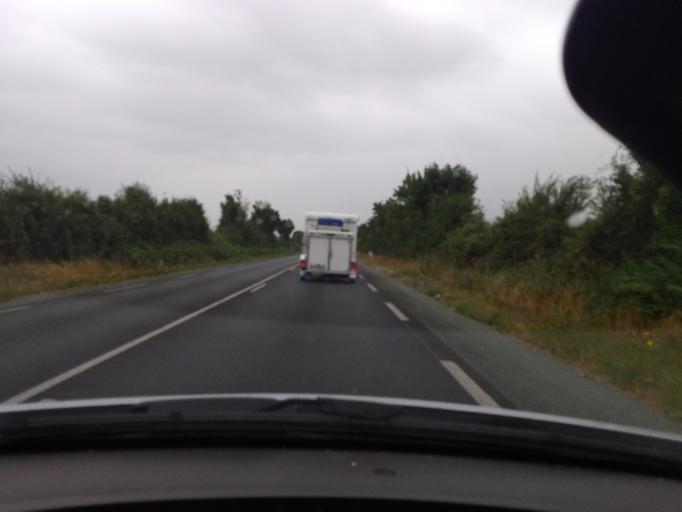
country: FR
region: Pays de la Loire
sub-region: Departement de la Vendee
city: Sainte-Gemme-la-Plaine
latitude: 46.5073
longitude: -1.0956
